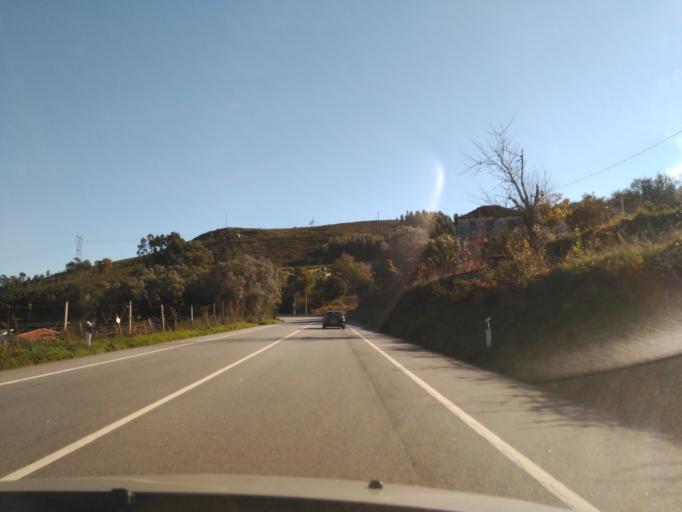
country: PT
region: Braga
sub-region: Amares
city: Amares
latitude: 41.5869
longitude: -8.3342
